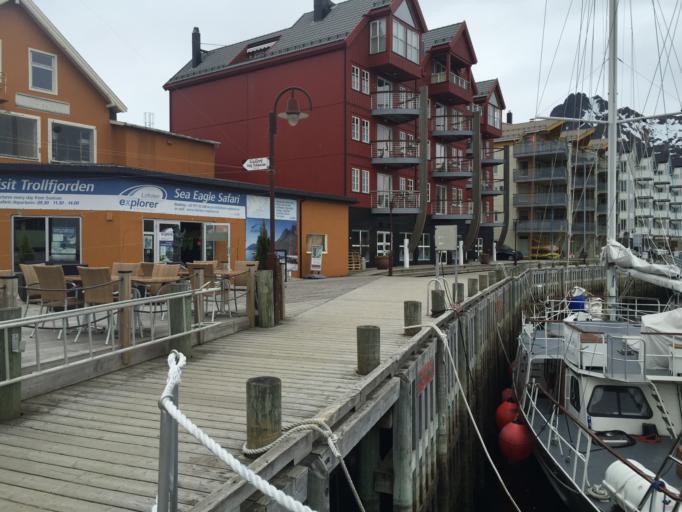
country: NO
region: Nordland
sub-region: Vagan
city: Svolvaer
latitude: 68.2326
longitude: 14.5668
